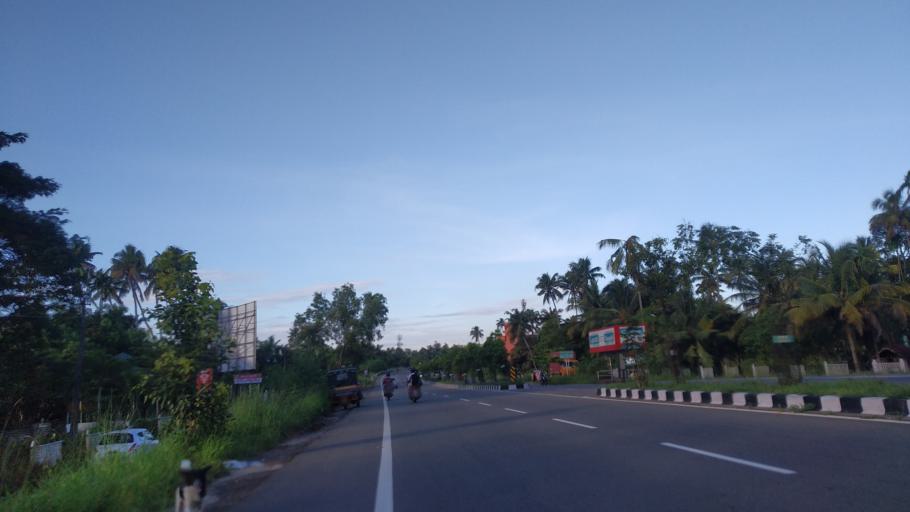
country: IN
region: Kerala
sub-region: Ernakulam
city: Elur
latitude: 10.0569
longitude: 76.2842
